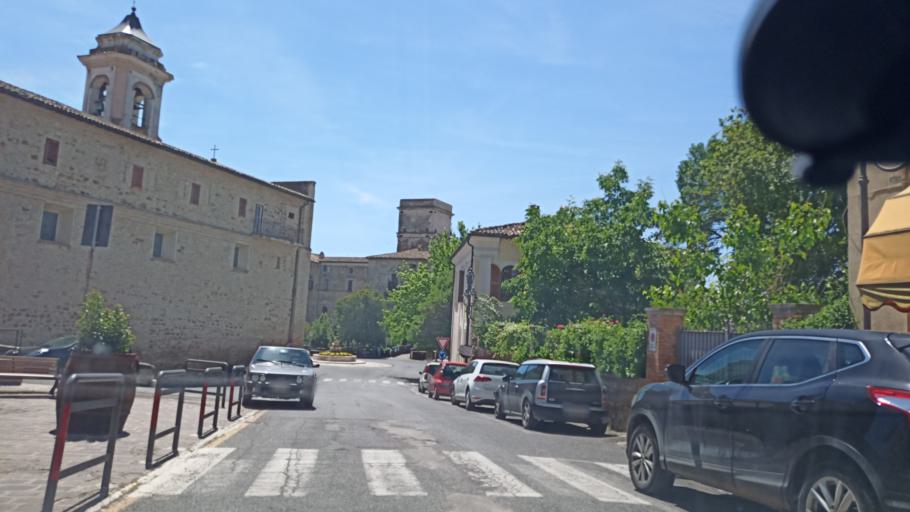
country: IT
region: Latium
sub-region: Provincia di Rieti
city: Stimigliano
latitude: 42.3001
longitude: 12.5655
